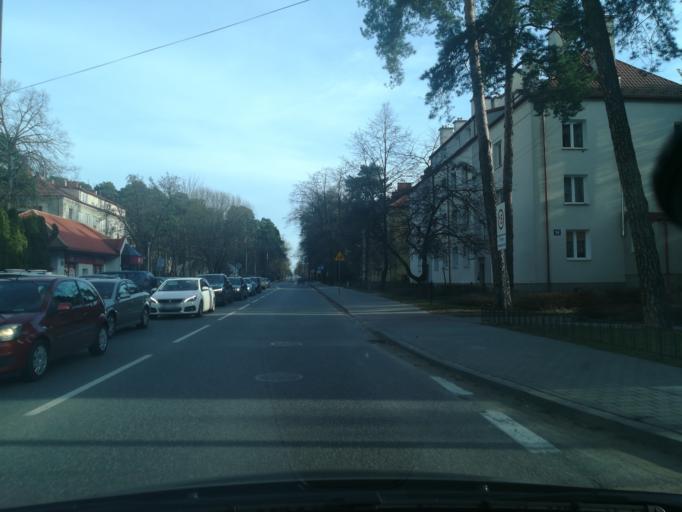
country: PL
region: Masovian Voivodeship
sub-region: Powiat piaseczynski
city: Konstancin-Jeziorna
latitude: 52.0877
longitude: 21.1244
